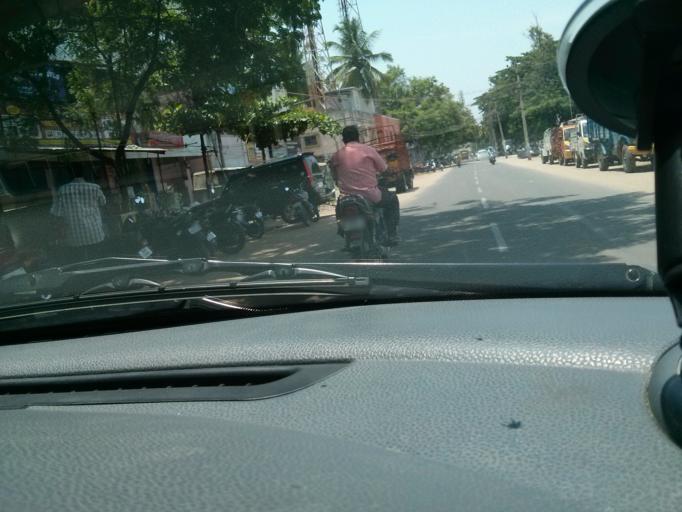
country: IN
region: Tamil Nadu
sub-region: Coimbatore
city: Coimbatore
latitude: 11.0344
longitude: 76.9655
